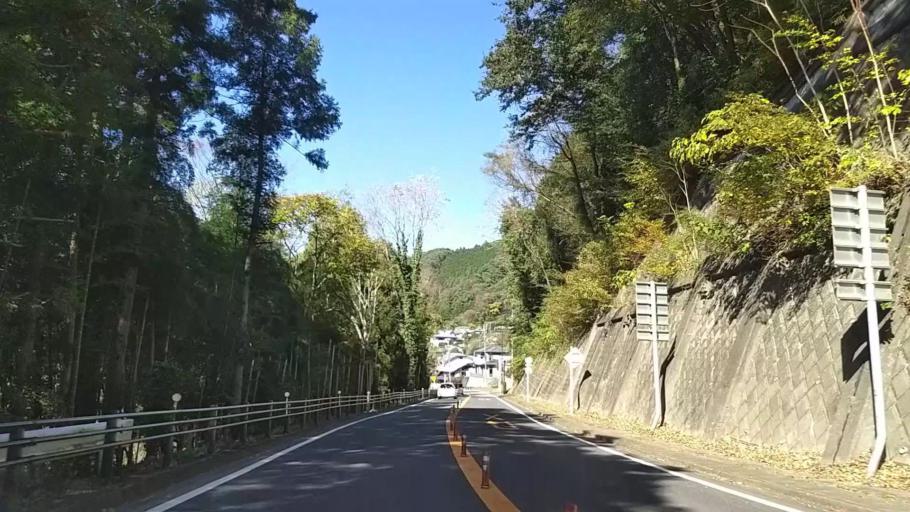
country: JP
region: Yamanashi
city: Uenohara
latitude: 35.6182
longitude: 139.2119
